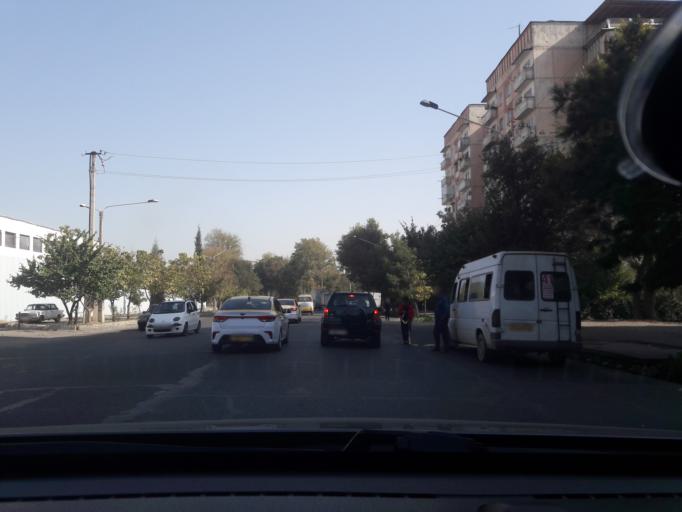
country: TJ
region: Dushanbe
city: Dushanbe
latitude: 38.5184
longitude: 68.7510
